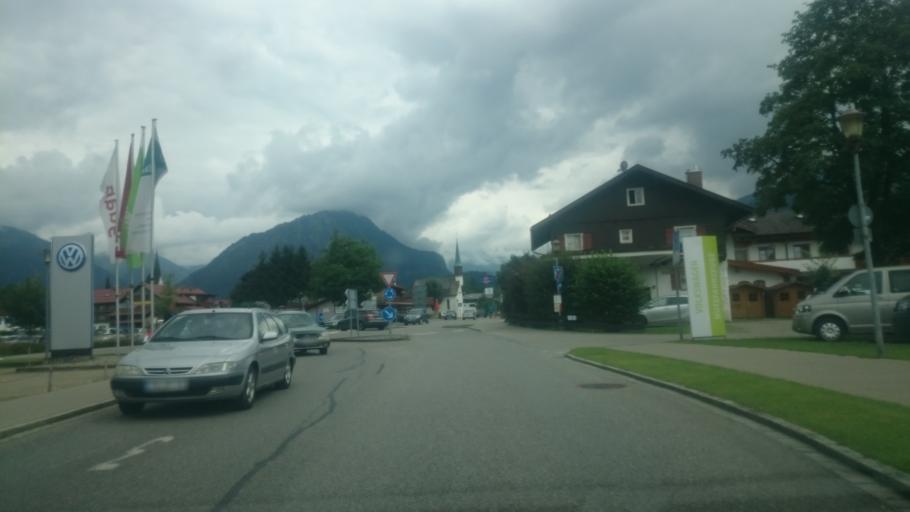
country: DE
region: Bavaria
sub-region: Swabia
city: Oberstdorf
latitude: 47.4128
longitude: 10.2754
